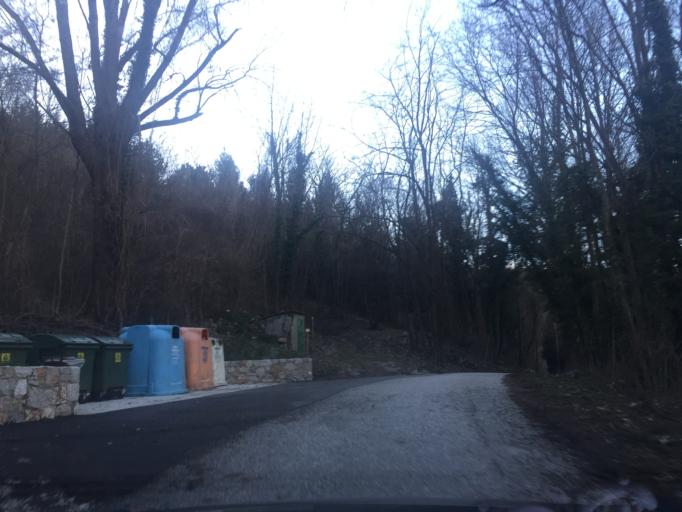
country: SI
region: Kanal
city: Deskle
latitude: 46.0369
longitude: 13.6636
